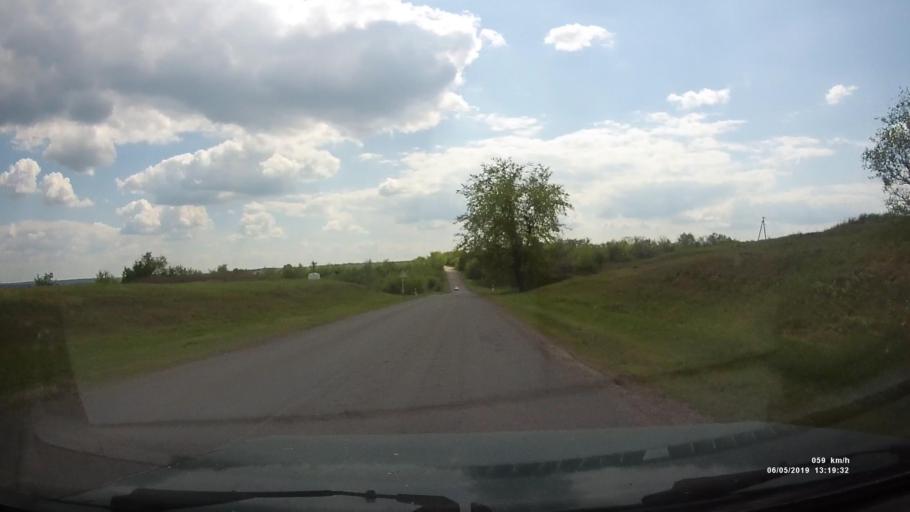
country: RU
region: Rostov
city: Ust'-Donetskiy
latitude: 47.7245
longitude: 40.9137
